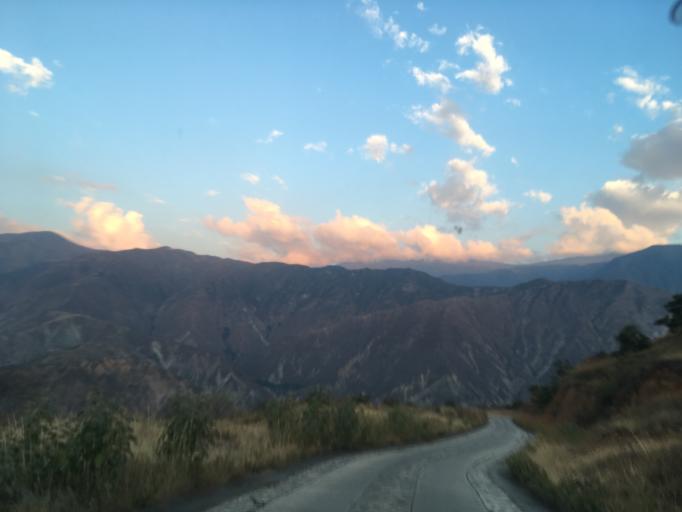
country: CO
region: Santander
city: Aratoca
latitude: 6.8015
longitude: -72.9949
